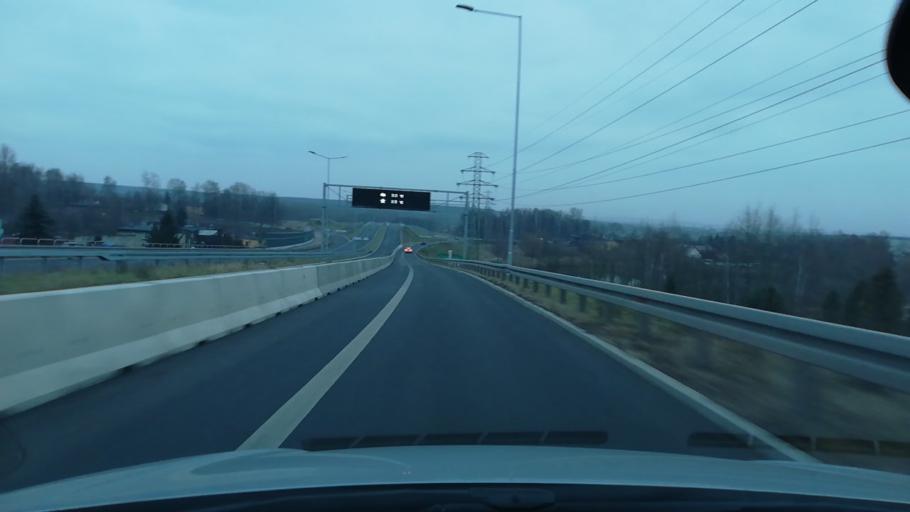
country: PL
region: Silesian Voivodeship
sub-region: Ruda Slaska
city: Ruda Slaska
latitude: 50.2763
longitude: 18.8452
